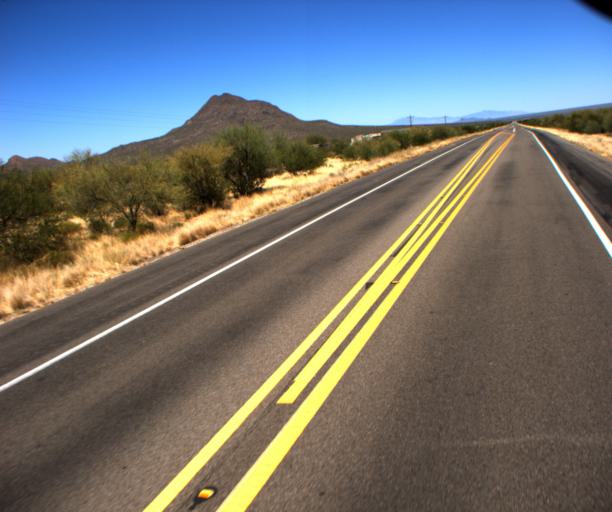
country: US
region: Arizona
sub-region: Pima County
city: Three Points
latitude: 32.0396
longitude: -111.4865
